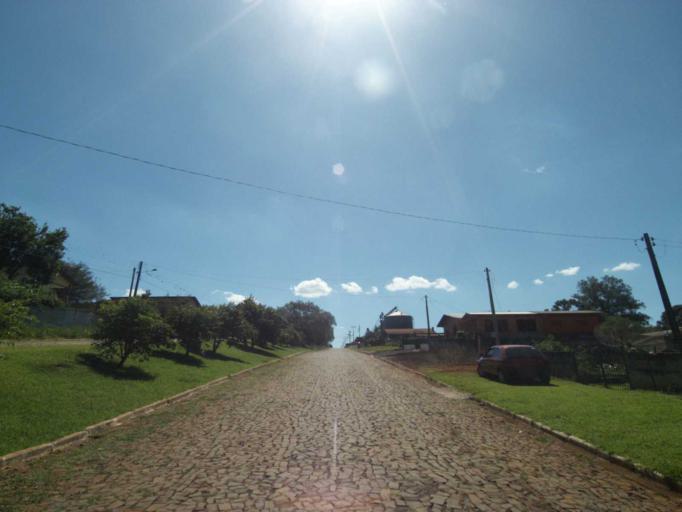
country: BR
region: Parana
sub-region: Laranjeiras Do Sul
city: Laranjeiras do Sul
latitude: -25.3811
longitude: -52.1970
